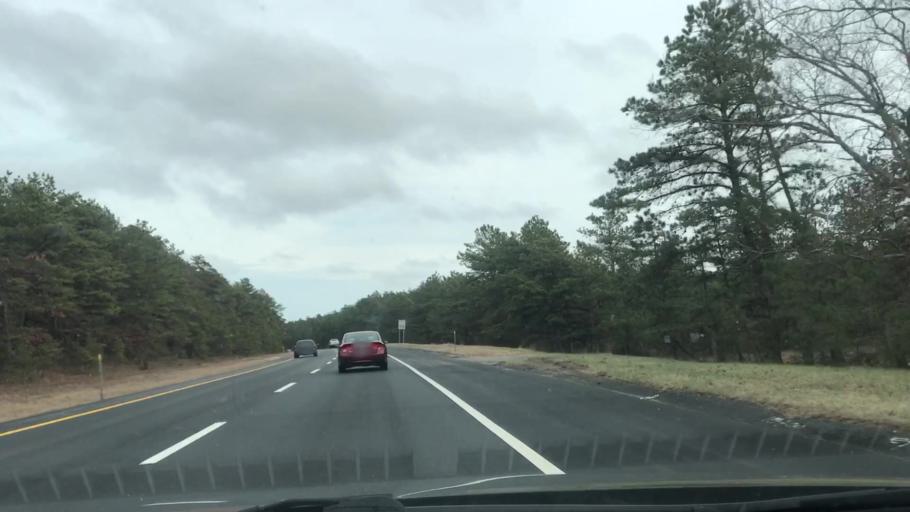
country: US
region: New York
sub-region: Suffolk County
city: Riverside
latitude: 40.9066
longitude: -72.7039
